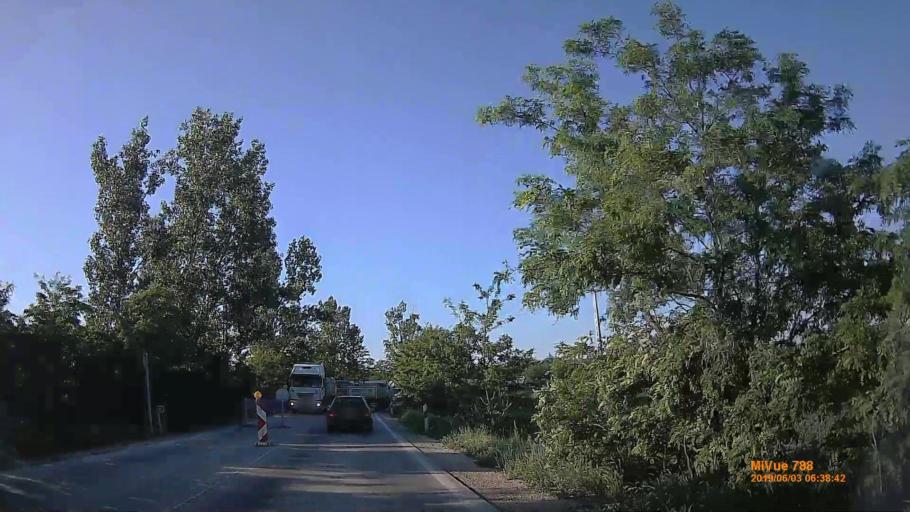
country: HU
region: Pest
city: Dunavarsany
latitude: 47.2932
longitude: 19.0952
